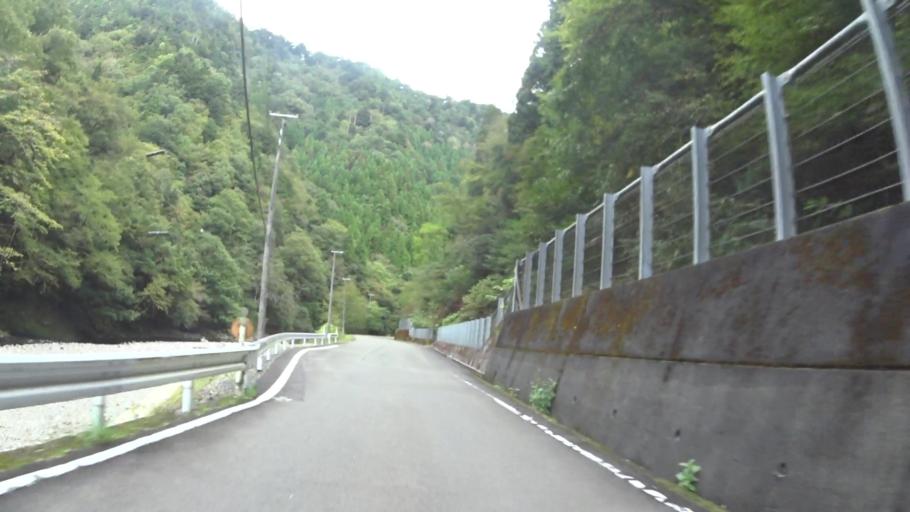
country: JP
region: Fukui
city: Obama
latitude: 35.2985
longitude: 135.6926
